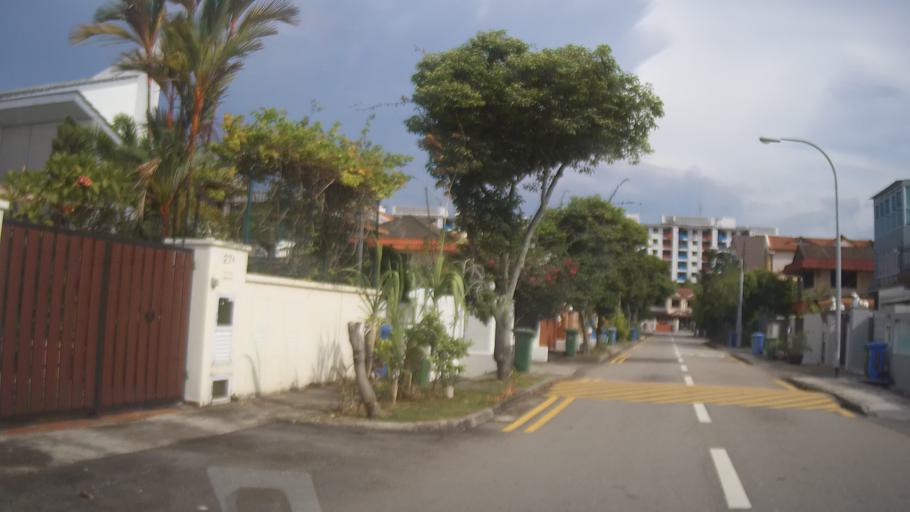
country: SG
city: Singapore
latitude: 1.3298
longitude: 103.8835
